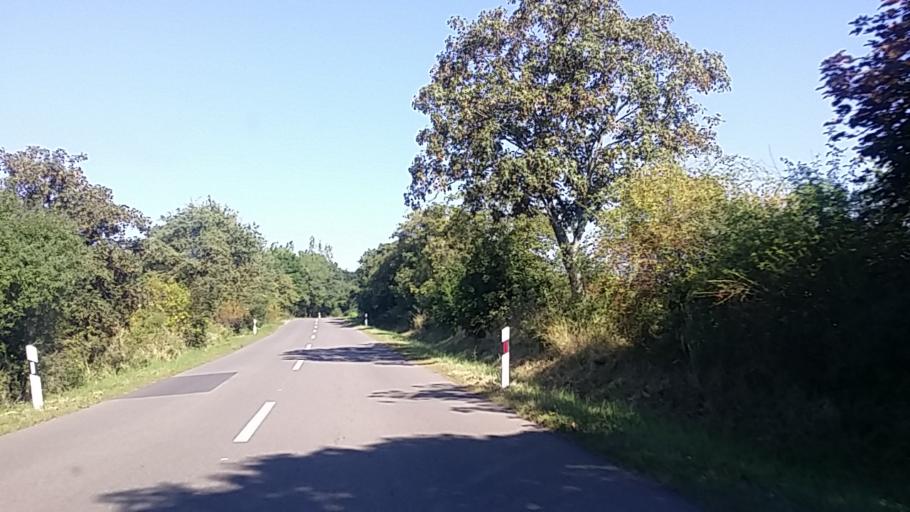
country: HU
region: Nograd
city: Bujak
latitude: 47.9313
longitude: 19.6114
